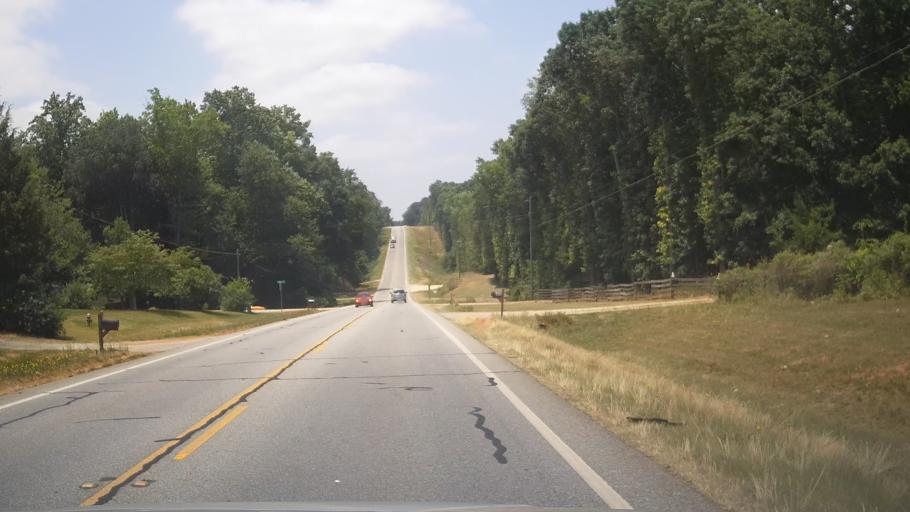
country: US
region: Georgia
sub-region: Jackson County
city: Commerce
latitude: 34.1893
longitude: -83.4045
